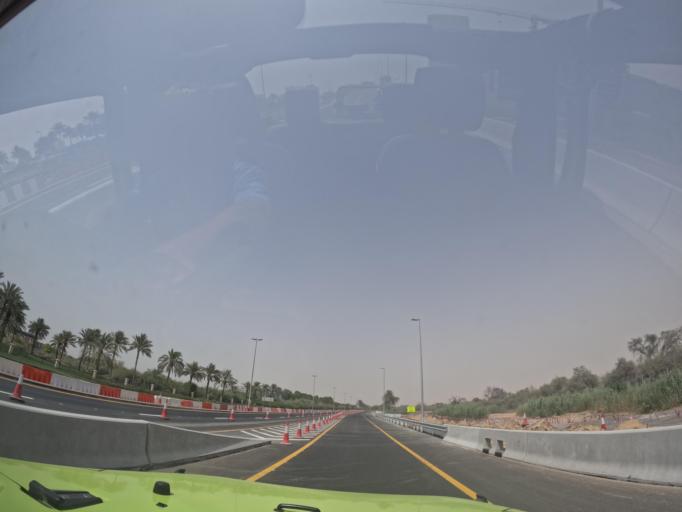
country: AE
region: Dubai
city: Dubai
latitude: 25.0993
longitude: 55.3879
